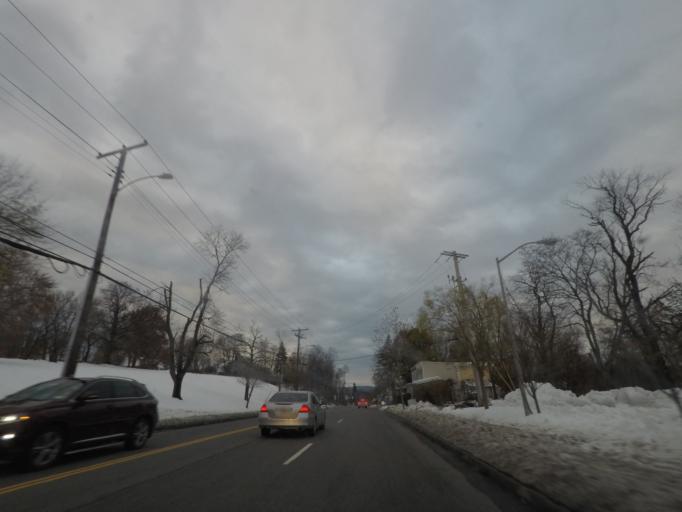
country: US
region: New York
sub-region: Orange County
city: Newburgh
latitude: 41.5124
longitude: -74.0203
